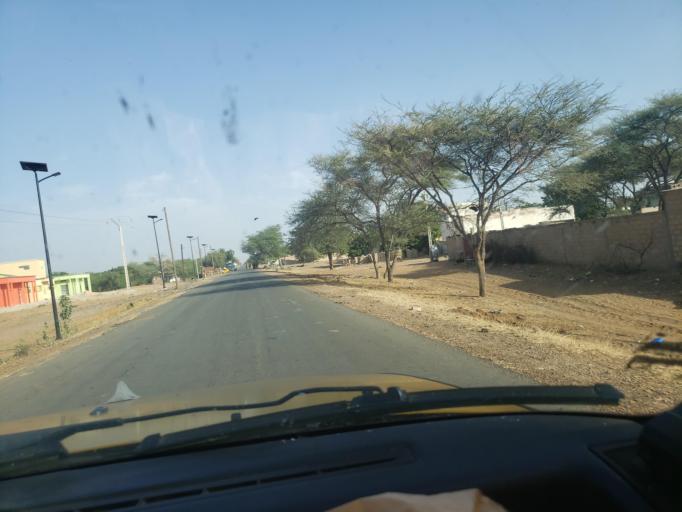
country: SN
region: Louga
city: Louga
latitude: 15.5121
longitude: -15.9915
